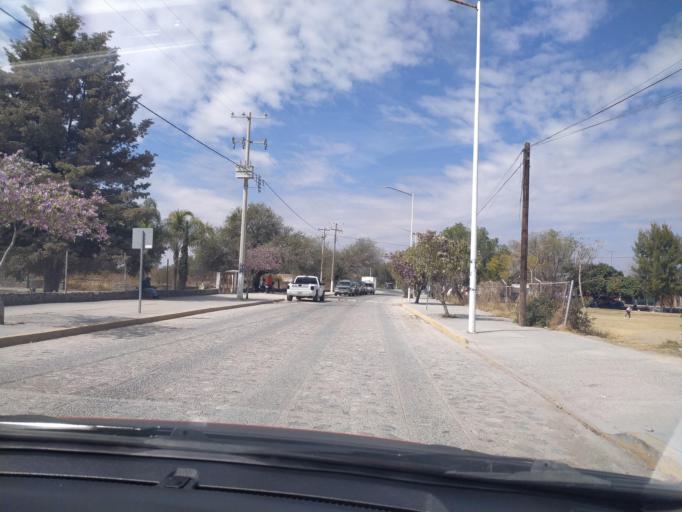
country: MX
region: Guanajuato
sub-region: San Francisco del Rincon
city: San Ignacio de Hidalgo
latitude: 20.8812
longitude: -101.8572
